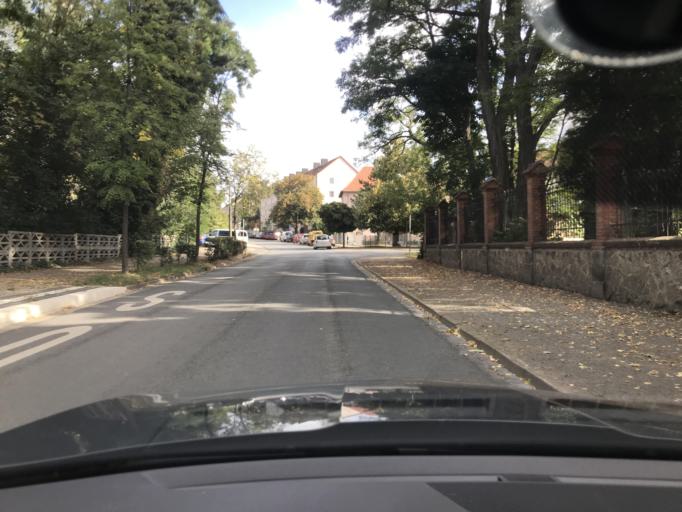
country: DE
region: Saxony-Anhalt
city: Quedlinburg
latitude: 51.7804
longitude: 11.1537
